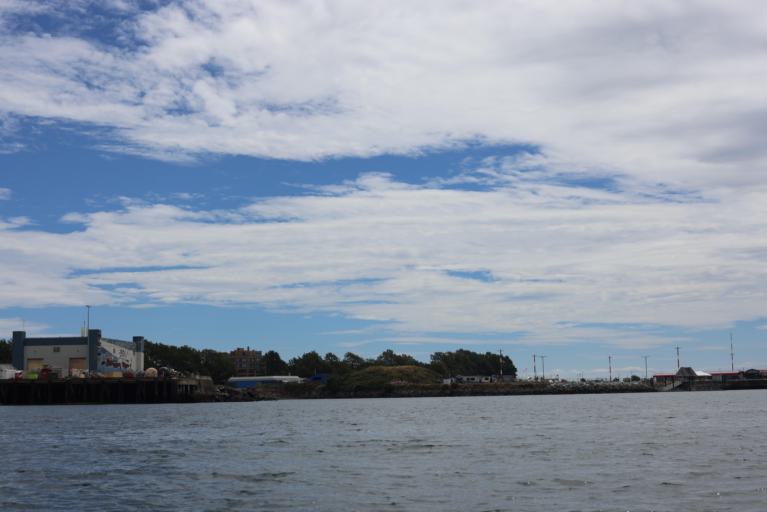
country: CA
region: British Columbia
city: Victoria
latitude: 48.4216
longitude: -123.3920
